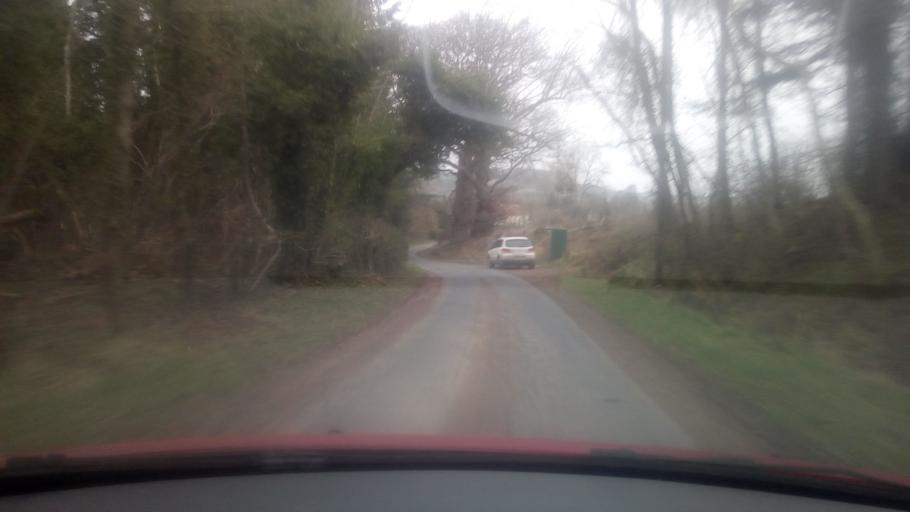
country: GB
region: Scotland
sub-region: The Scottish Borders
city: Hawick
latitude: 55.4520
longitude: -2.6856
